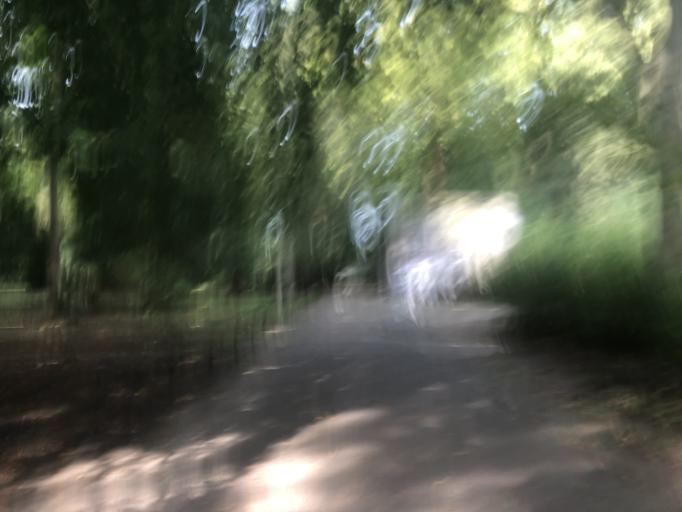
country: DE
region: Mecklenburg-Vorpommern
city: Rostock
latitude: 54.0844
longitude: 12.1210
